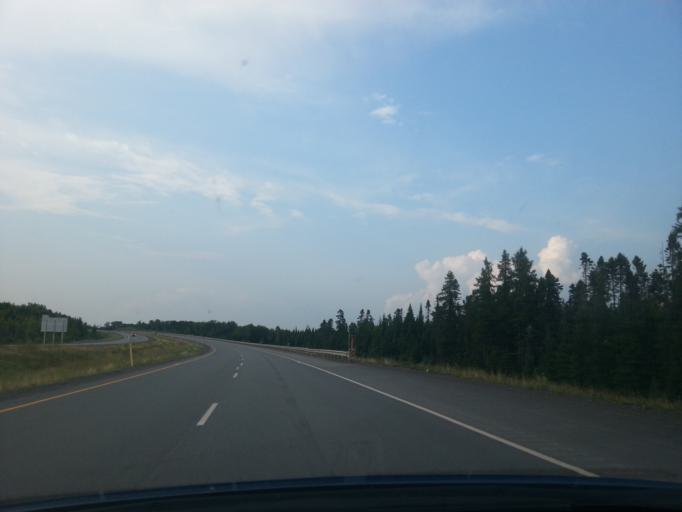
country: CA
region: New Brunswick
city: Harrison Brook
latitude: 47.2059
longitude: -67.9302
